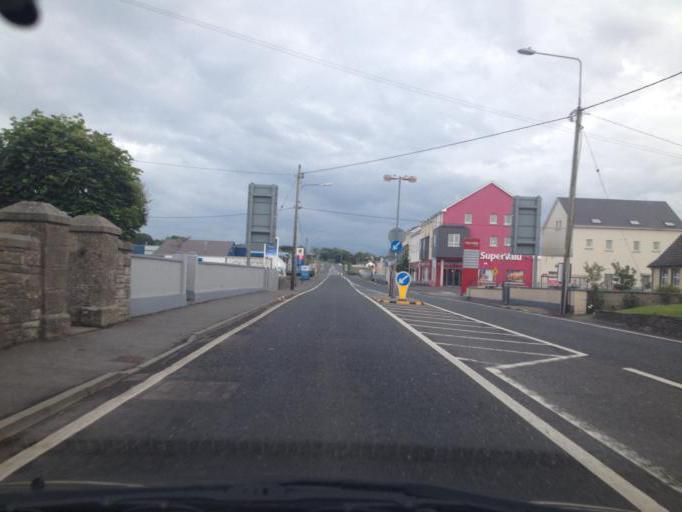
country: IE
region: Connaught
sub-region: Sligo
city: Sligo
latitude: 54.3915
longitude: -8.5270
